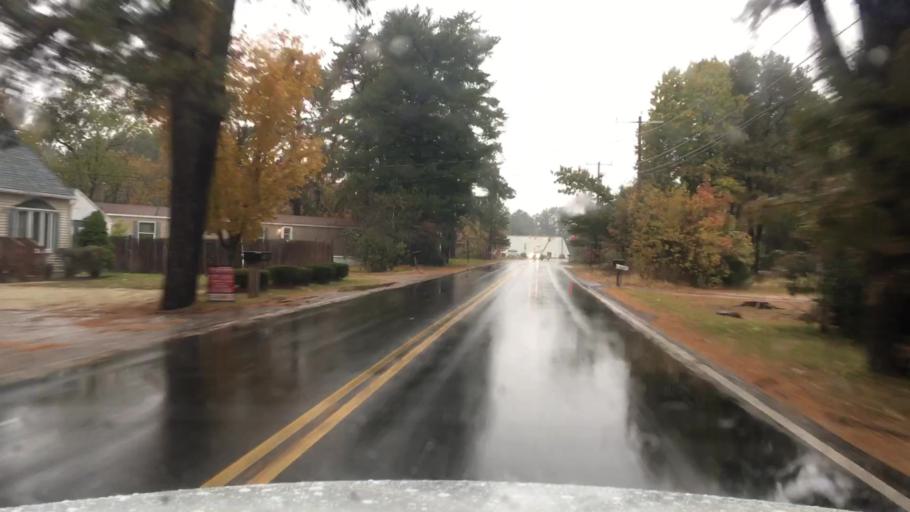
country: US
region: New Hampshire
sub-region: Strafford County
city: Rochester
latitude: 43.3450
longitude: -70.9725
